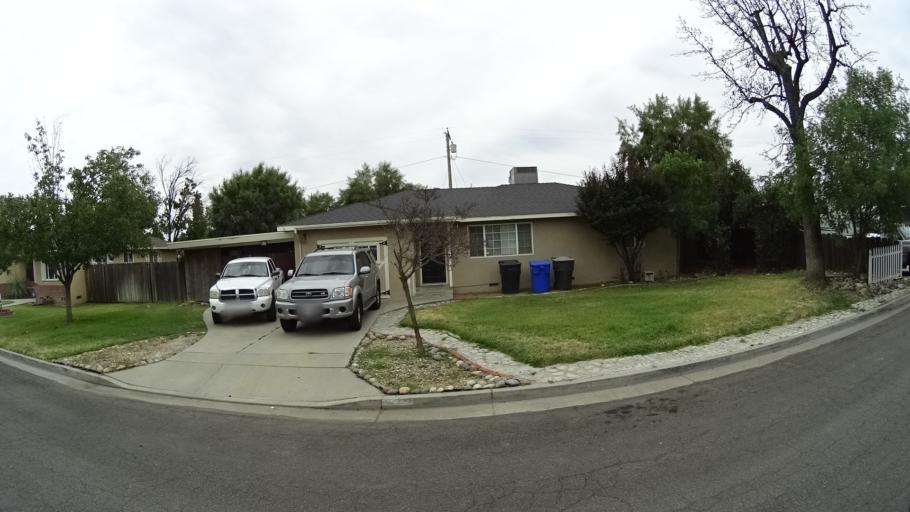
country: US
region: California
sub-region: Kings County
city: Hanford
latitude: 36.3485
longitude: -119.6497
